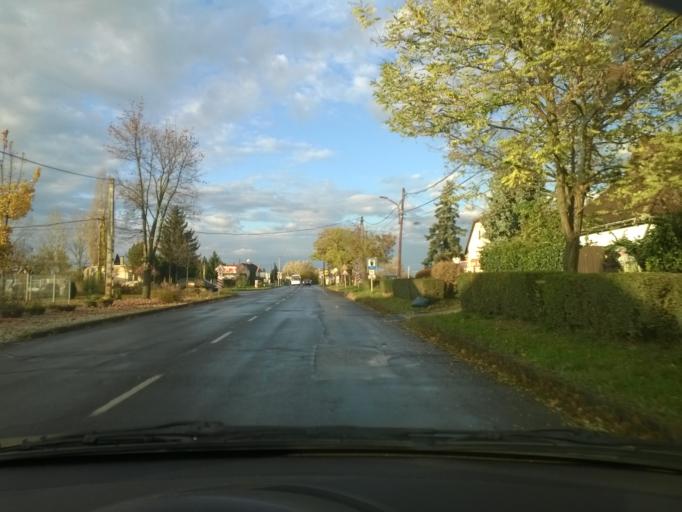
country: HU
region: Bacs-Kiskun
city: Kalocsa
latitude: 46.5375
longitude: 18.9855
